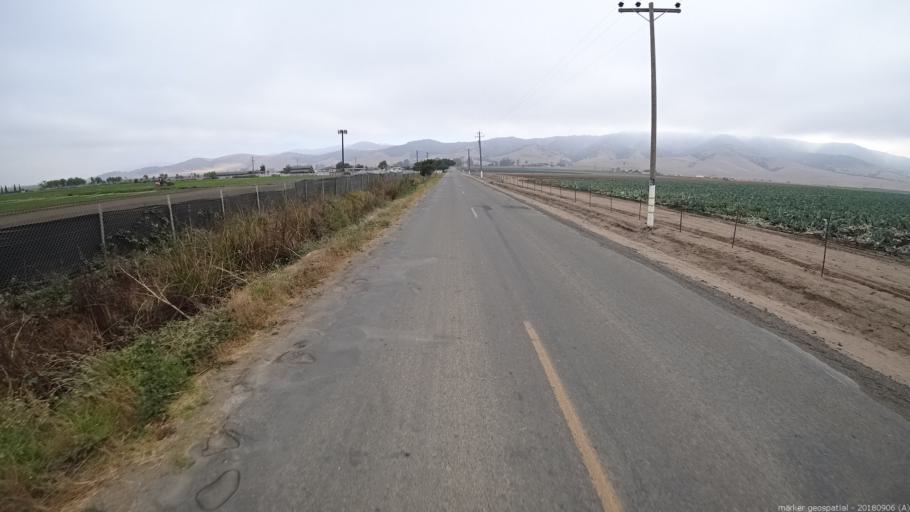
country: US
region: California
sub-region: Monterey County
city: Chualar
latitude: 36.6577
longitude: -121.5566
